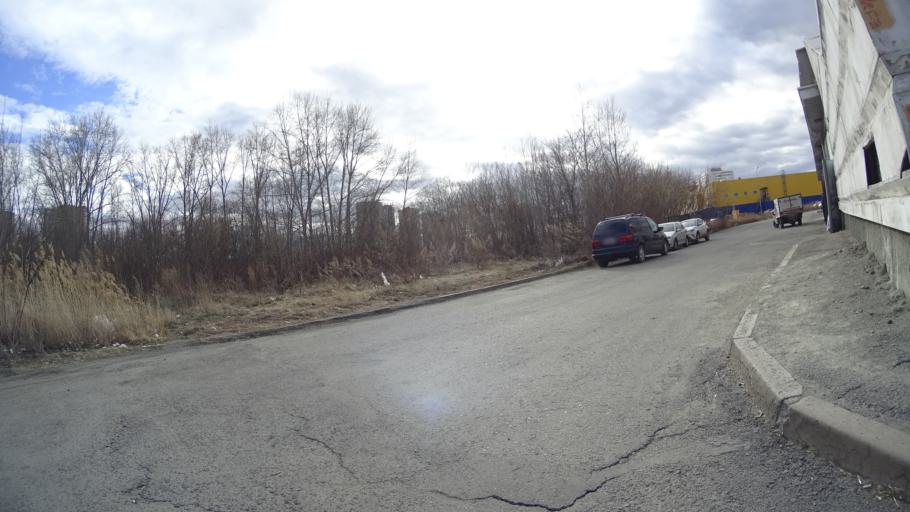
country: RU
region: Chelyabinsk
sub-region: Gorod Chelyabinsk
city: Chelyabinsk
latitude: 55.1745
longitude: 61.3788
